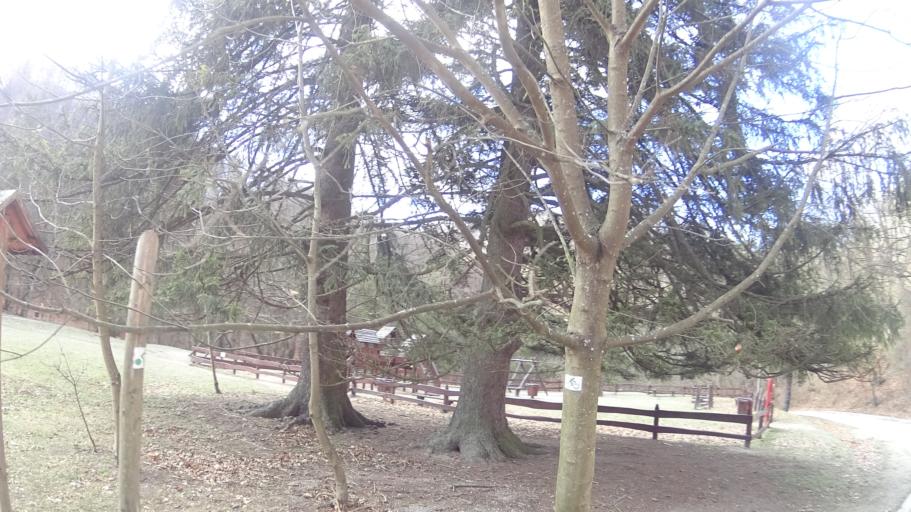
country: HU
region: Heves
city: Szilvasvarad
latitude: 48.0760
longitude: 20.4120
